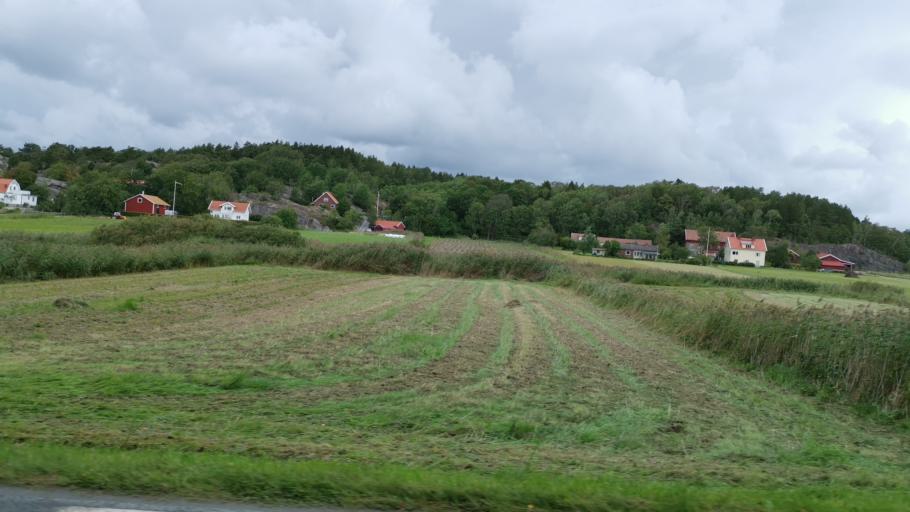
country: SE
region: Vaestra Goetaland
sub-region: Tjorns Kommun
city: Skaerhamn
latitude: 58.0401
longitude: 11.6023
